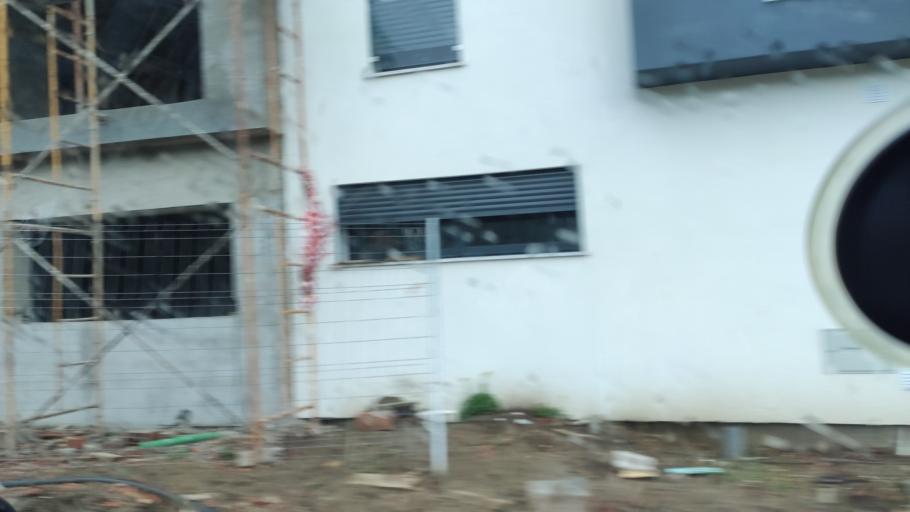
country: PT
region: Beja
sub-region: Beja
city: Beja
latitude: 38.0156
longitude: -7.8518
